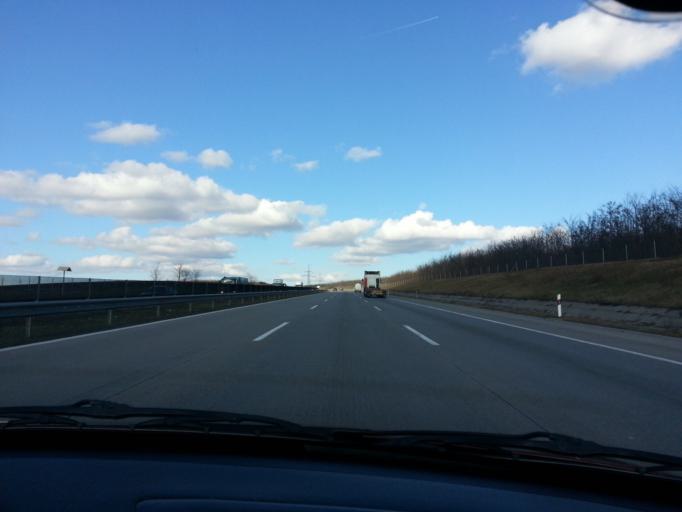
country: HU
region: Pest
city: Ecser
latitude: 47.4476
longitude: 19.3322
